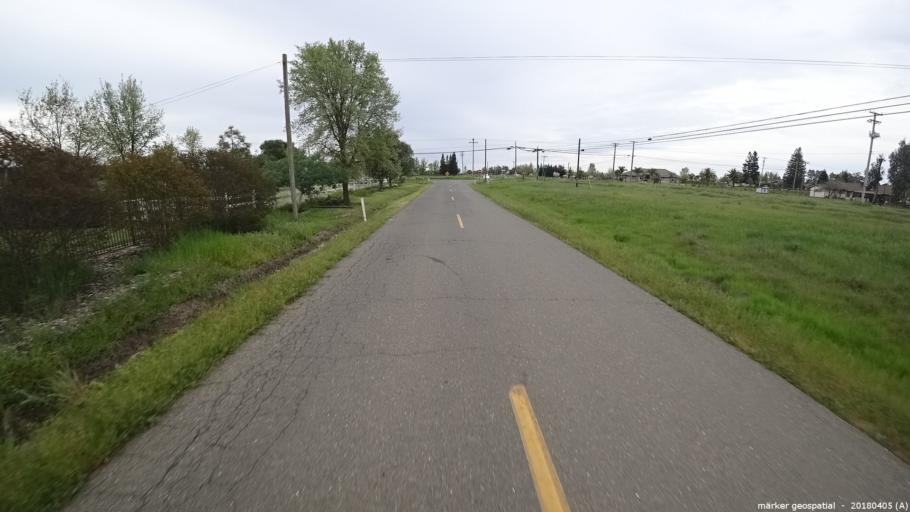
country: US
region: California
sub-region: Sacramento County
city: Herald
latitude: 38.2925
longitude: -121.2443
